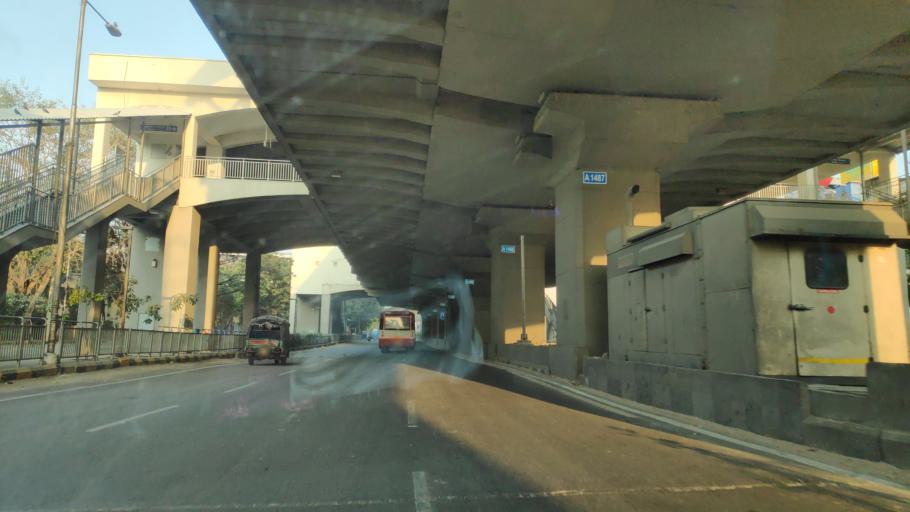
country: IN
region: Telangana
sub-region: Rangareddi
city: Gaddi Annaram
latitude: 17.3708
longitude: 78.5125
